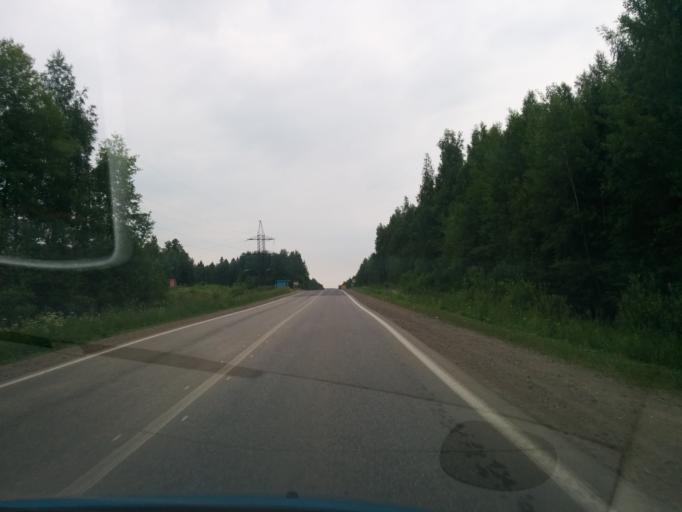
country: RU
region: Perm
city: Perm
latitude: 58.1441
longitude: 56.2644
